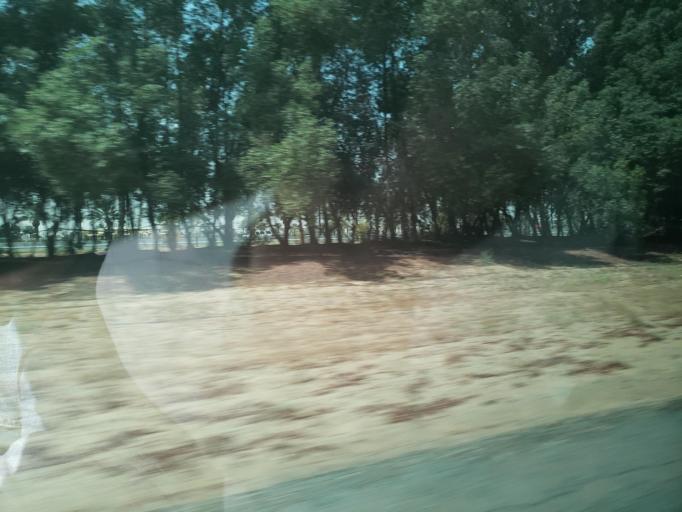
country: AE
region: Ash Shariqah
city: Sharjah
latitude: 25.3225
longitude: 55.5016
